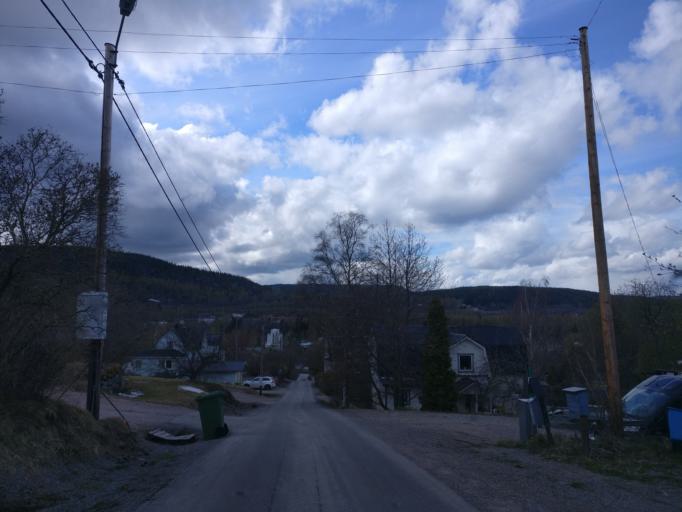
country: SE
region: Vaesternorrland
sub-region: Sundsvalls Kommun
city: Skottsund
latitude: 62.3063
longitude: 17.3923
